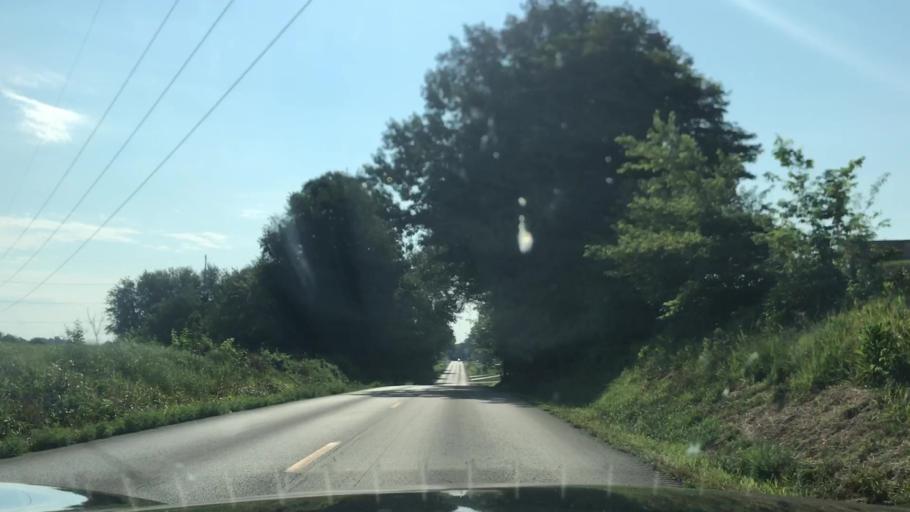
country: US
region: Kentucky
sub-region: Hart County
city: Horse Cave
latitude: 37.1674
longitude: -85.8156
